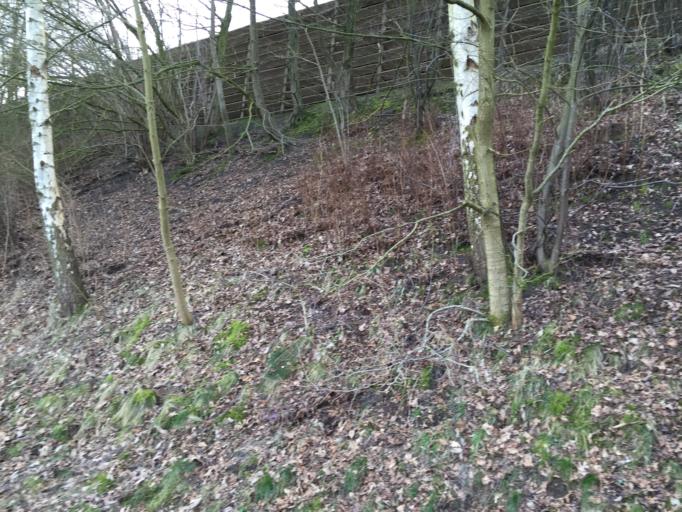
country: DE
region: Lower Saxony
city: Oldenburg
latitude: 53.1628
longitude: 8.2307
